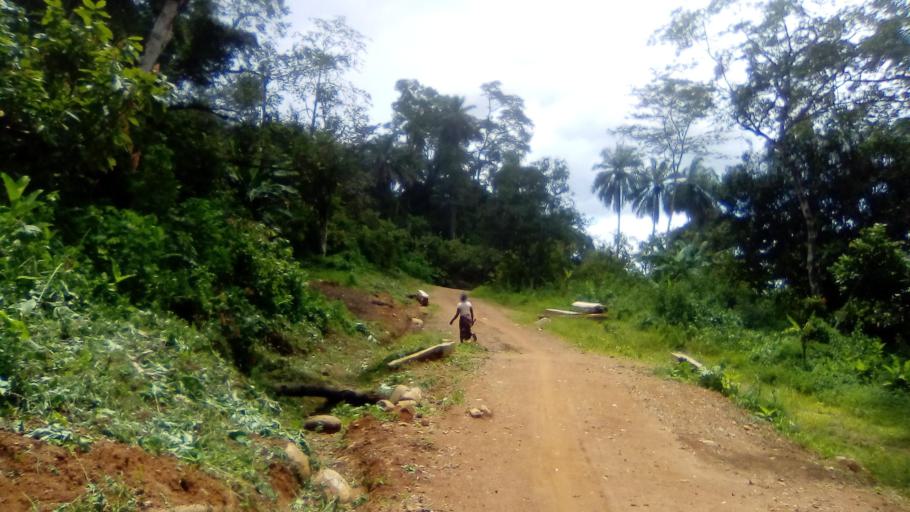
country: SL
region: Eastern Province
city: Giehun
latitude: 8.5042
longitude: -10.9053
